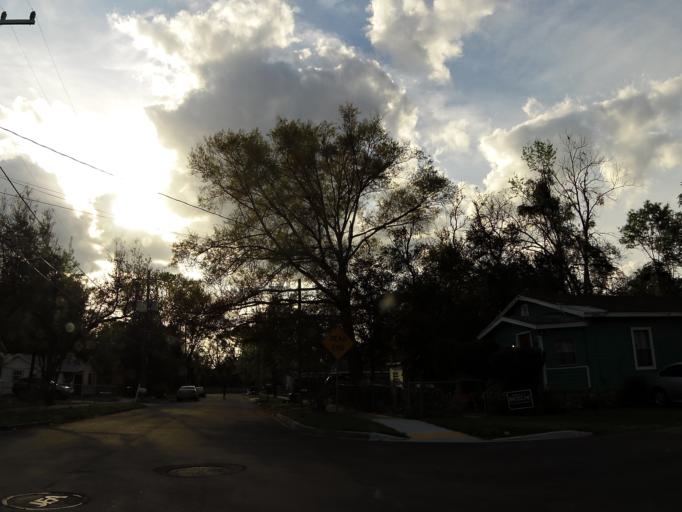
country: US
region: Florida
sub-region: Duval County
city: Jacksonville
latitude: 30.3559
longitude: -81.6899
